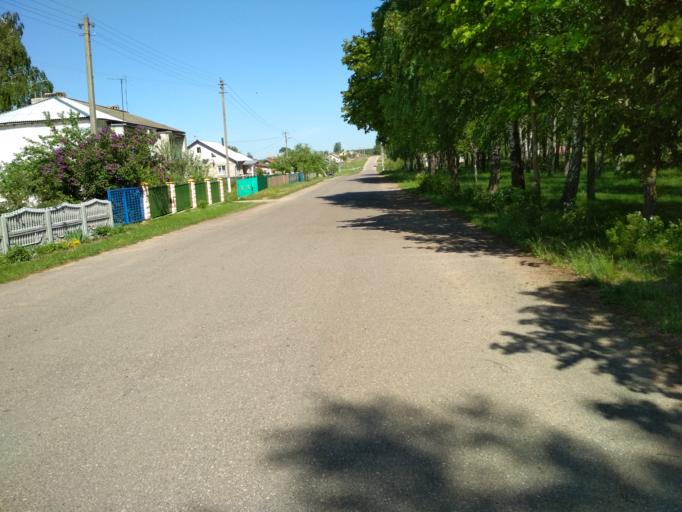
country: BY
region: Grodnenskaya
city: Mir
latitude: 53.3813
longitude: 26.3651
